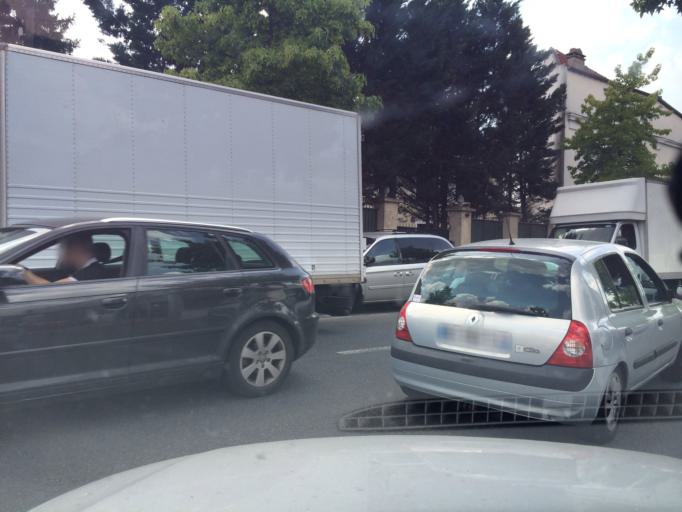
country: FR
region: Ile-de-France
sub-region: Departement du Val-de-Marne
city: Saint-Maur-des-Fosses
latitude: 48.7984
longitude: 2.4764
